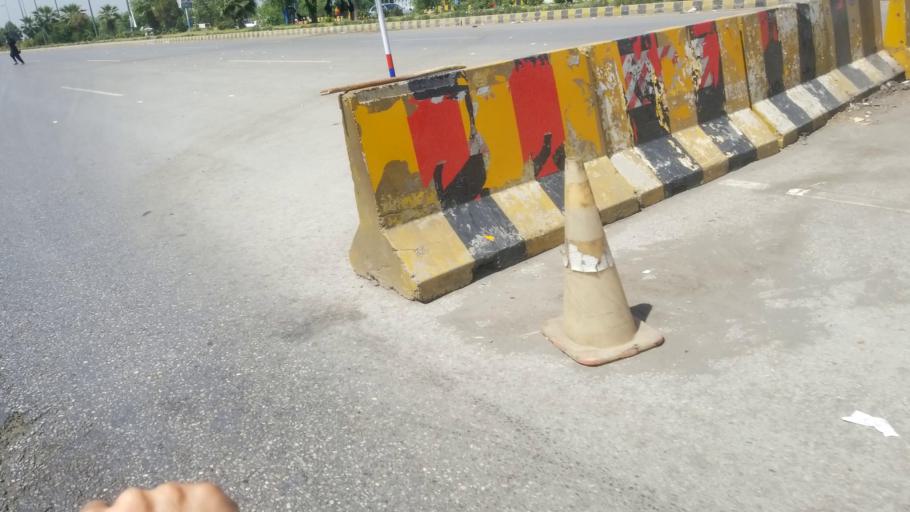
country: PK
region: Khyber Pakhtunkhwa
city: Peshawar
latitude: 34.0298
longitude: 71.6633
